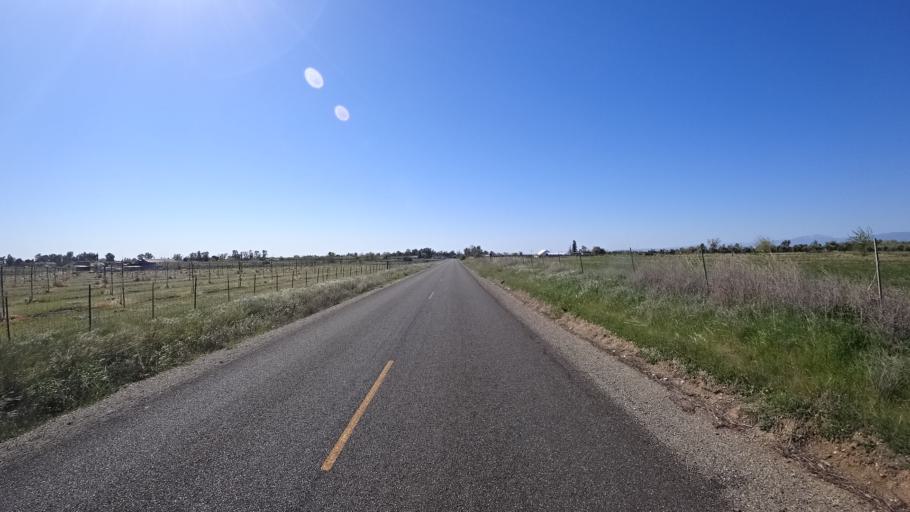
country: US
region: California
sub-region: Glenn County
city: Orland
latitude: 39.7311
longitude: -122.2158
